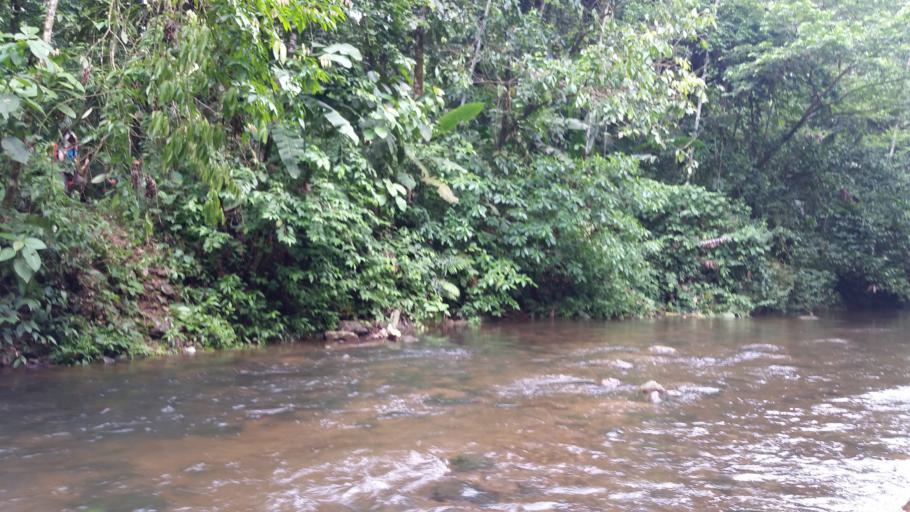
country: NI
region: Atlantico Norte (RAAN)
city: Bonanza
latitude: 14.0230
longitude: -84.7395
